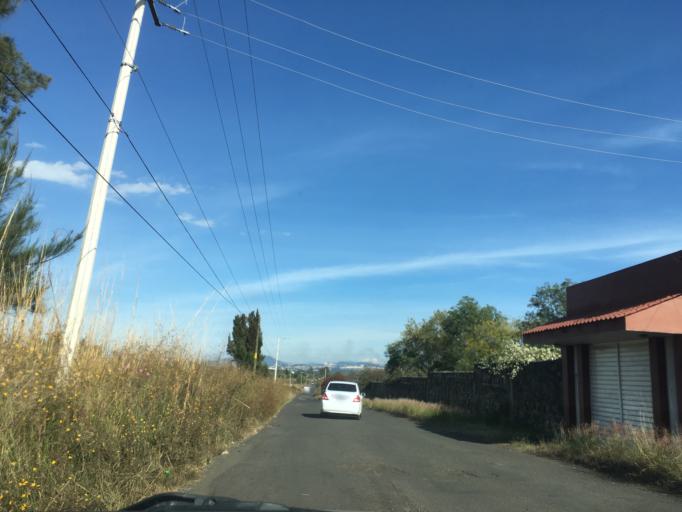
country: MX
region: Michoacan
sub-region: Morelia
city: La Mintzita (Piedra Dura)
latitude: 19.6494
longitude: -101.2879
